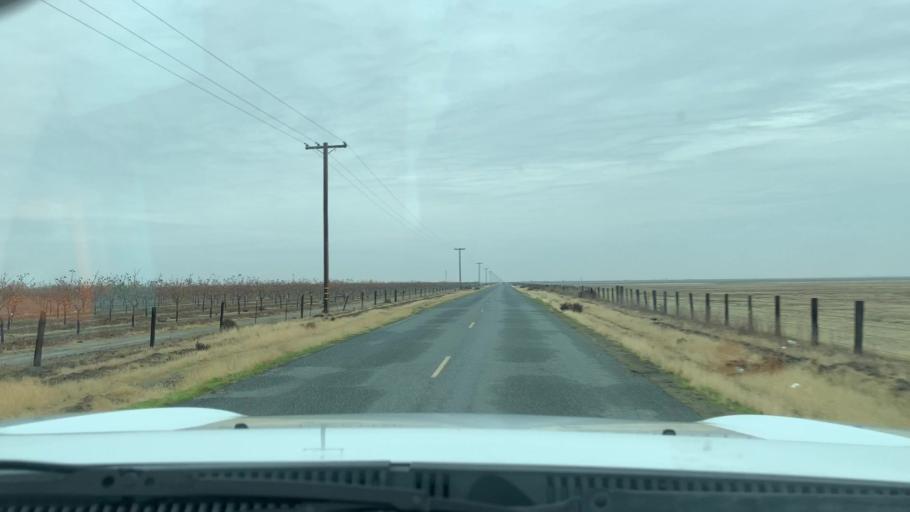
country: US
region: California
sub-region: Tulare County
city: Alpaugh
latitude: 35.7608
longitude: -119.5591
